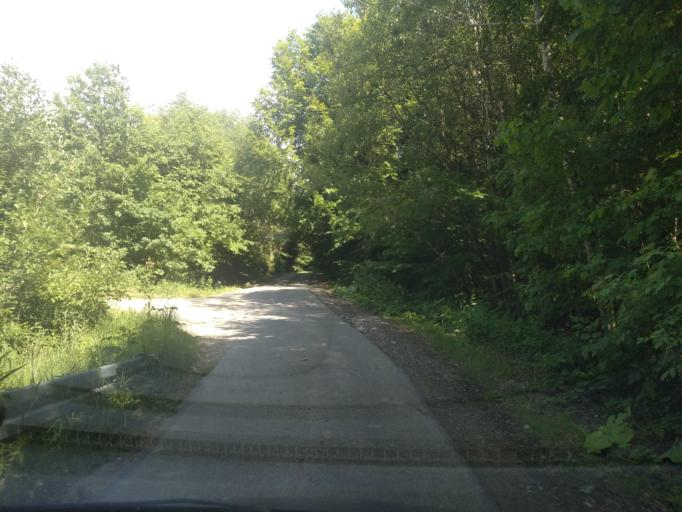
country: PL
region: Subcarpathian Voivodeship
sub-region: Powiat krosnienski
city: Iwonicz-Zdroj
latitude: 49.5441
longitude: 21.7802
